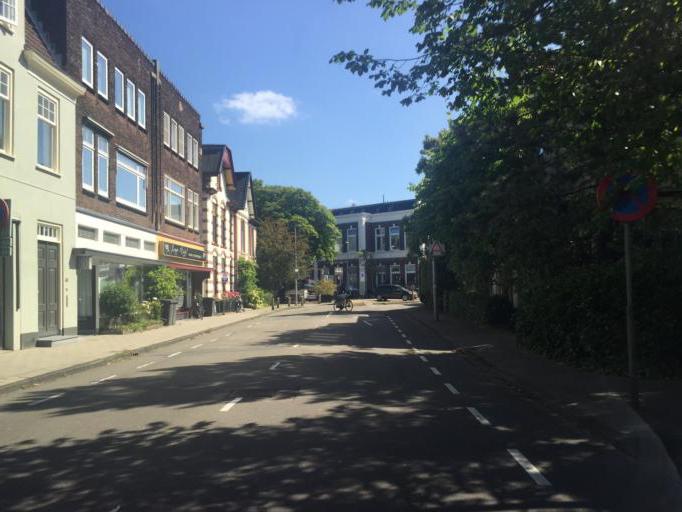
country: NL
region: North Holland
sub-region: Gemeente Haarlem
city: Haarlem
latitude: 52.3758
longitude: 4.6238
